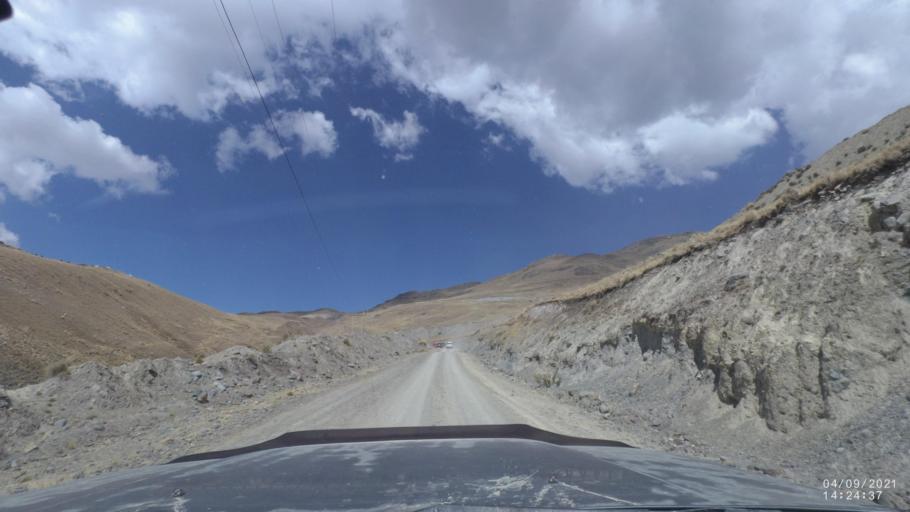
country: BO
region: Cochabamba
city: Sipe Sipe
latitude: -17.2414
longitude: -66.4090
